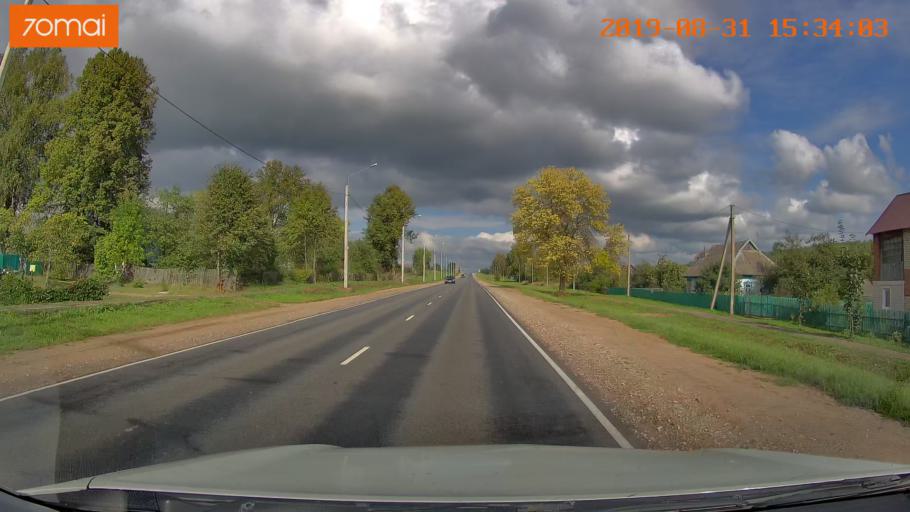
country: RU
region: Kaluga
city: Mosal'sk
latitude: 54.5985
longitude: 34.7129
